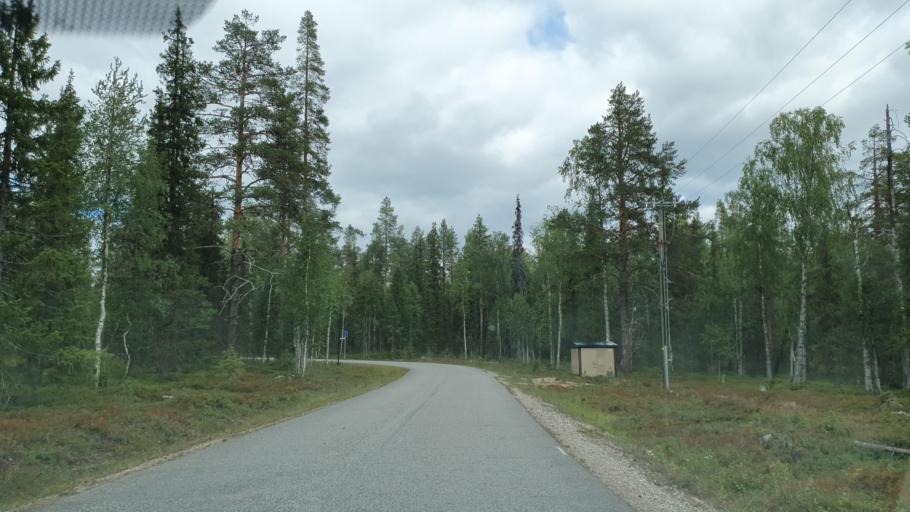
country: FI
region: Lapland
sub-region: Tunturi-Lappi
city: Kolari
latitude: 67.5493
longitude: 24.2780
